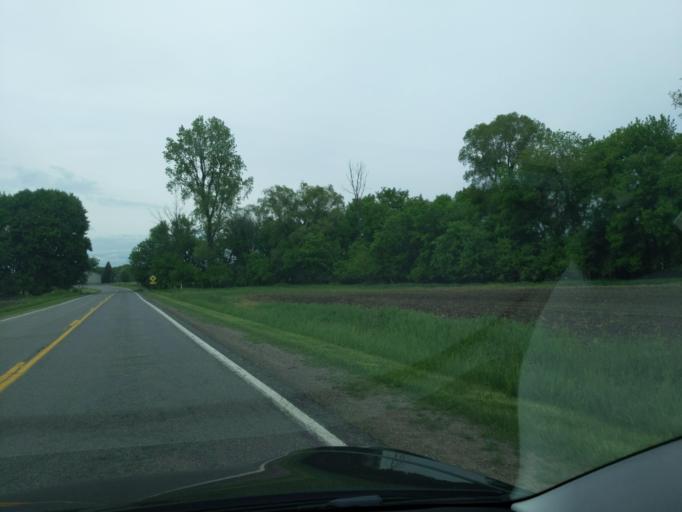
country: US
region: Michigan
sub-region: Ingham County
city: Mason
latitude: 42.5507
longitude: -84.4234
